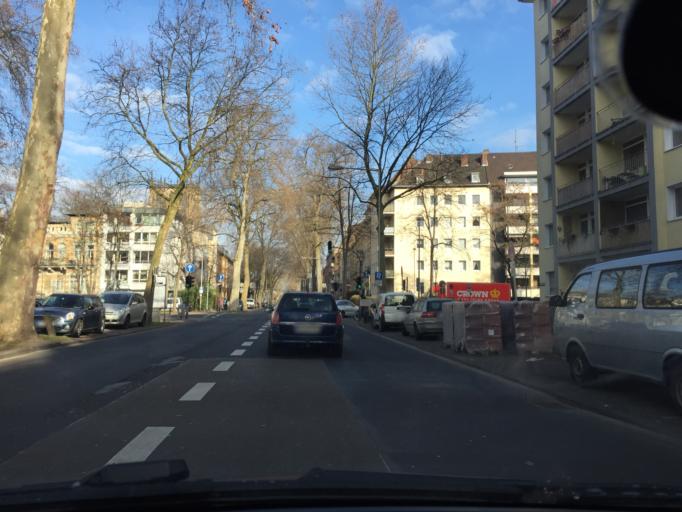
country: DE
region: North Rhine-Westphalia
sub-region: Regierungsbezirk Koln
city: Neustadt/Sued
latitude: 50.9202
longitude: 6.9506
